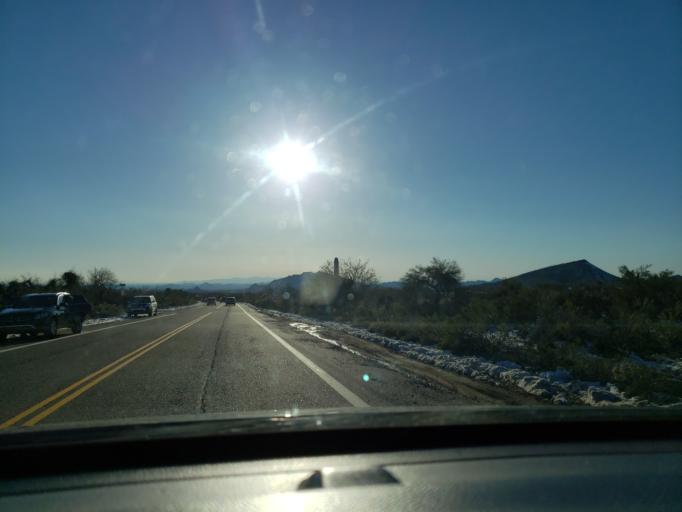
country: US
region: Arizona
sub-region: Maricopa County
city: Carefree
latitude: 33.8406
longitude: -111.8458
